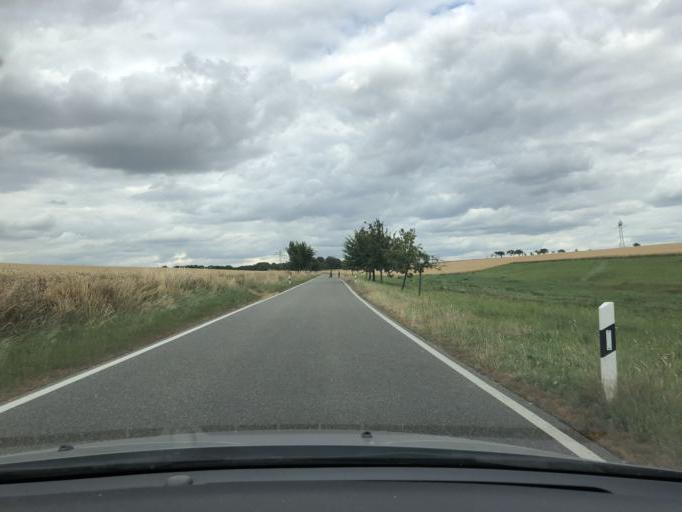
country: DE
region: Thuringia
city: Langenleuba-Niederhain
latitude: 51.0173
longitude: 12.6181
